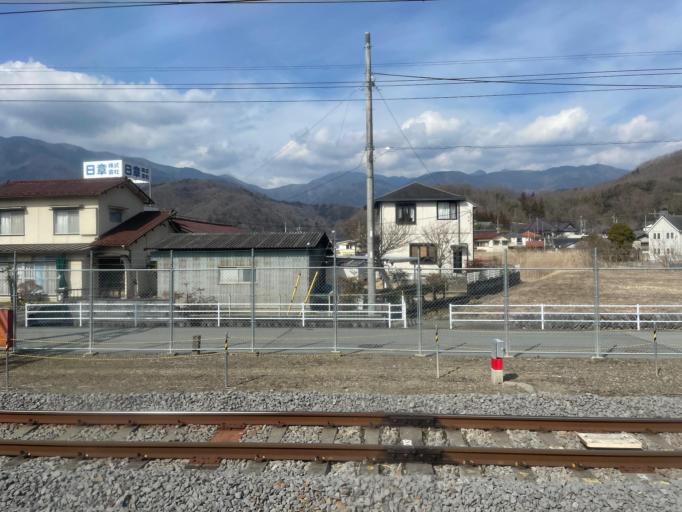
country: JP
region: Yamanashi
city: Ryuo
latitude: 35.4936
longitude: 138.4634
